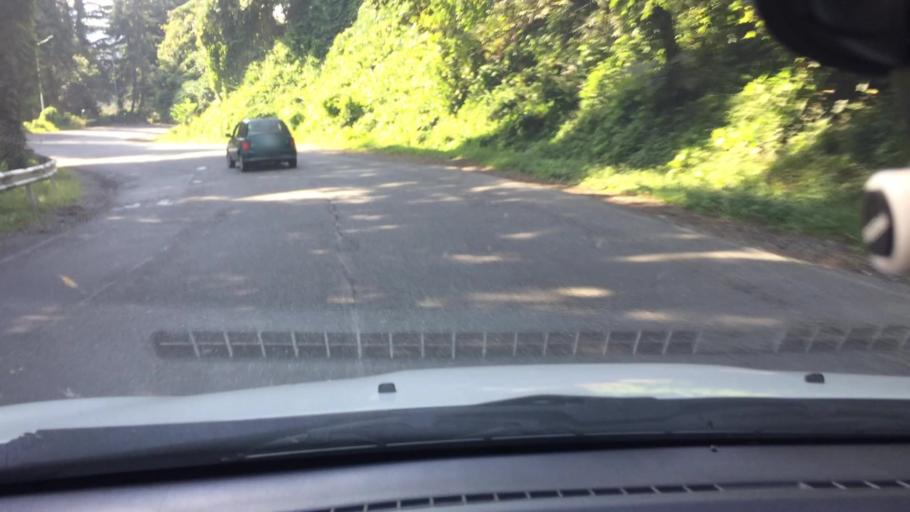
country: GE
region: Ajaria
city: Kobuleti
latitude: 41.7549
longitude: 41.7489
